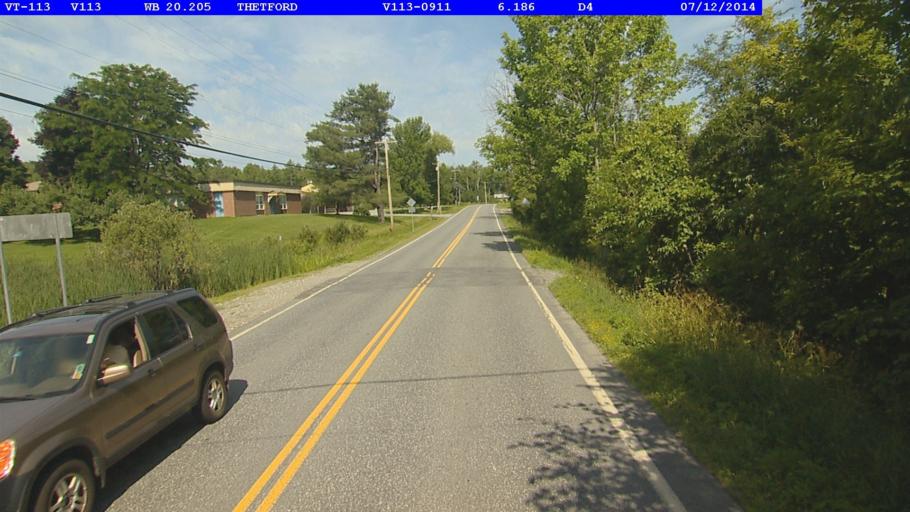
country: US
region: New Hampshire
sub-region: Grafton County
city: Lyme
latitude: 43.8194
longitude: -72.2299
